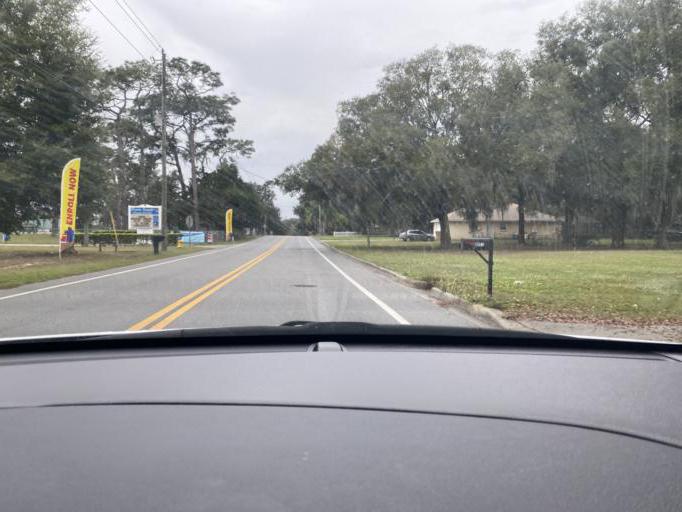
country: US
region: Florida
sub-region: Lake County
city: Groveland
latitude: 28.5748
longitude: -81.8572
